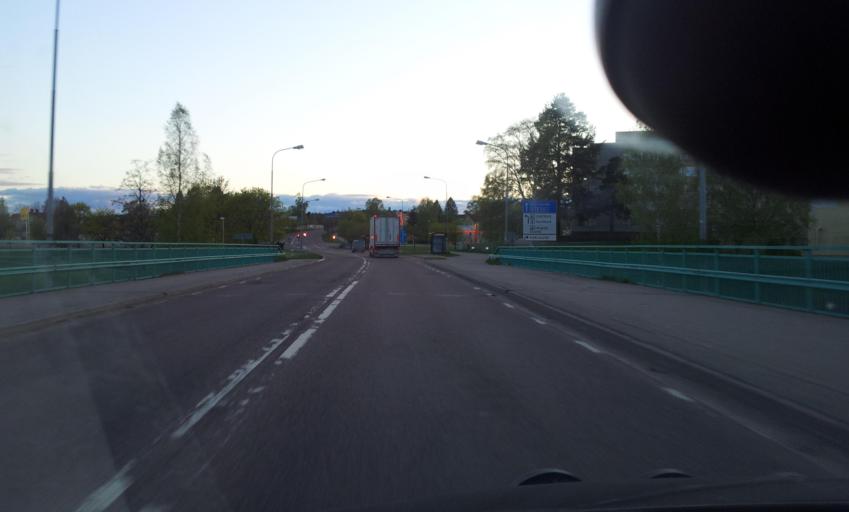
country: SE
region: Gaevleborg
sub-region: Bollnas Kommun
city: Bollnas
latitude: 61.3563
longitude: 16.4039
